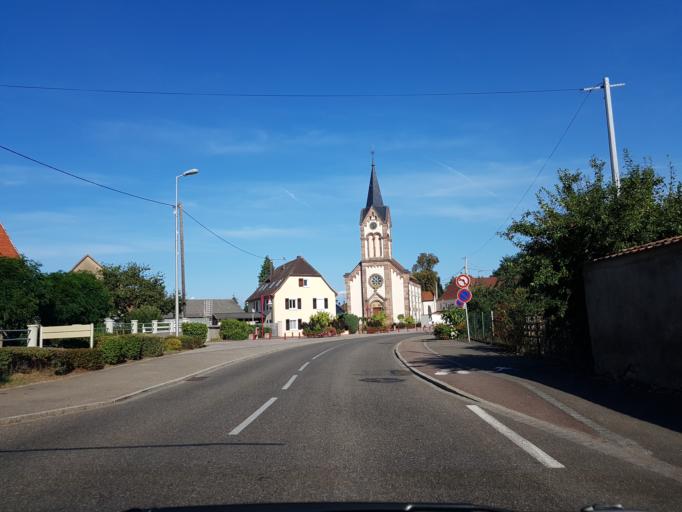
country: FR
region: Alsace
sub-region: Departement du Haut-Rhin
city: Pulversheim
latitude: 47.8383
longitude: 7.2975
